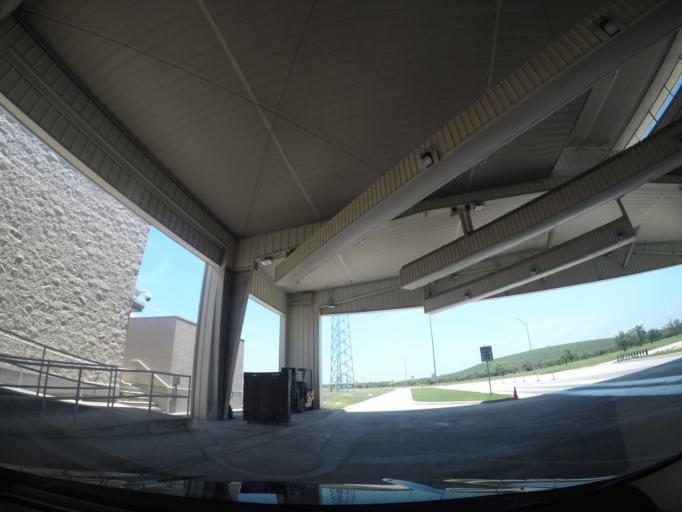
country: US
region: Texas
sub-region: Uvalde County
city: Uvalde Estates
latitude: 29.2161
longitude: -99.9424
